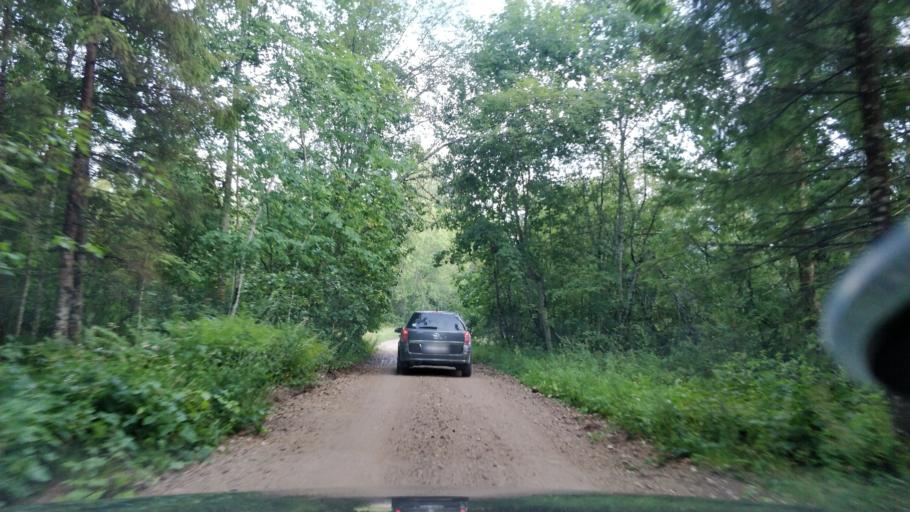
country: LV
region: Incukalns
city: Incukalns
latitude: 57.0984
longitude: 24.7758
